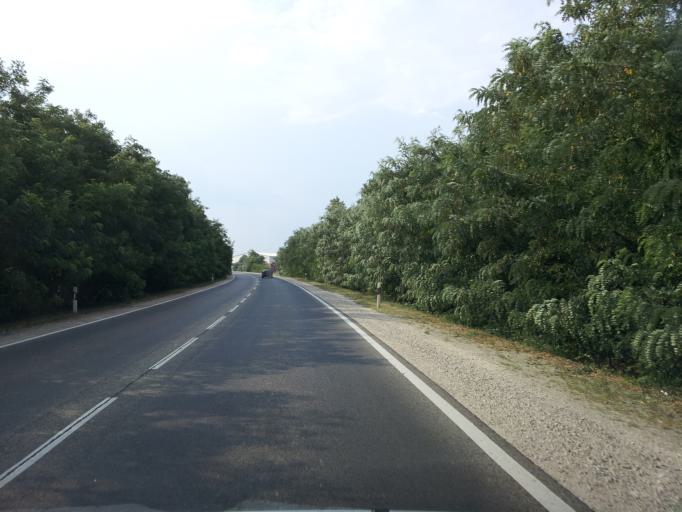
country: HU
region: Pest
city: Dunaharaszti
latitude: 47.3585
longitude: 19.1231
